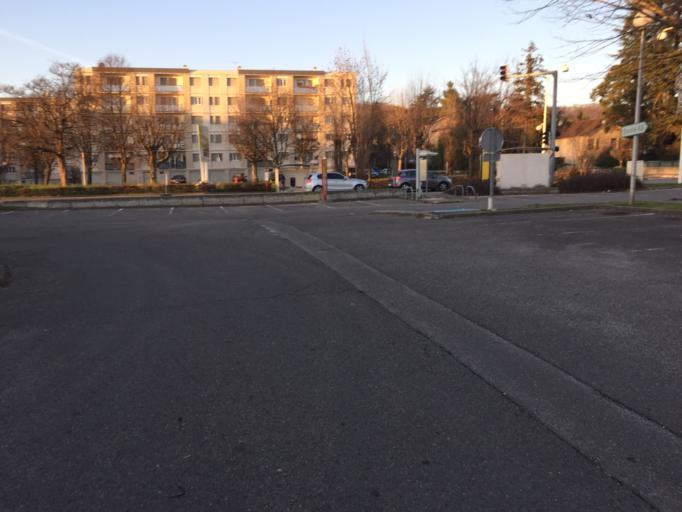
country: FR
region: Rhone-Alpes
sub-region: Departement de l'Ain
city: Saint-Maurice-de-Beynost
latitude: 45.8298
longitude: 4.9815
